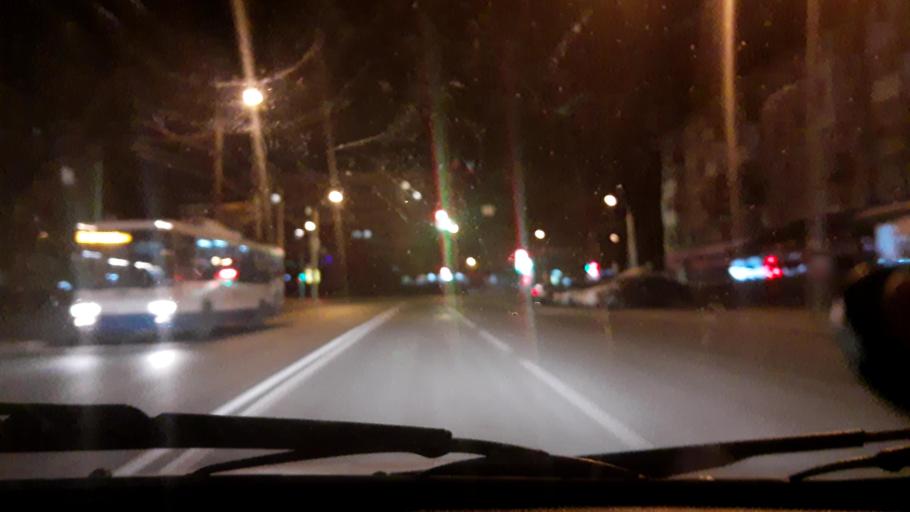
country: RU
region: Bashkortostan
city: Ufa
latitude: 54.8101
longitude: 56.1165
